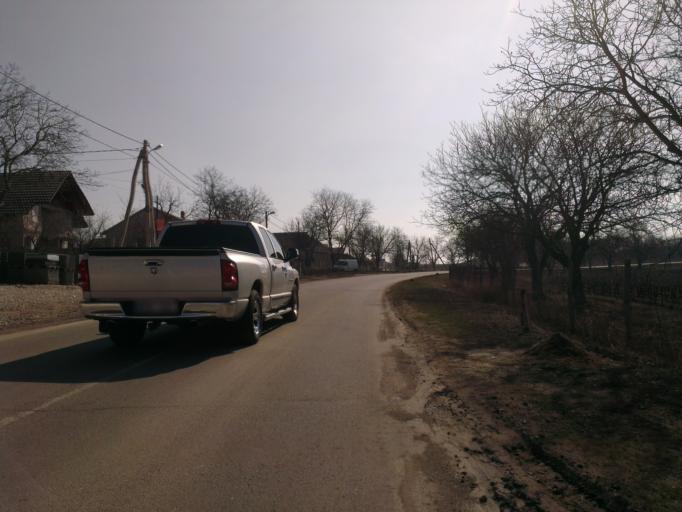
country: MD
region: Chisinau
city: Cricova
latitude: 47.1347
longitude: 28.8569
